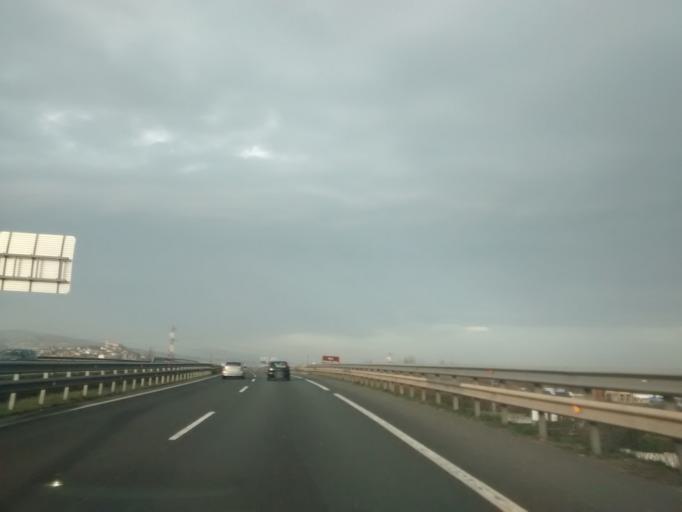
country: ES
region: Basque Country
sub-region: Provincia de Alava
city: Gasteiz / Vitoria
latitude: 42.8507
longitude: -2.7473
